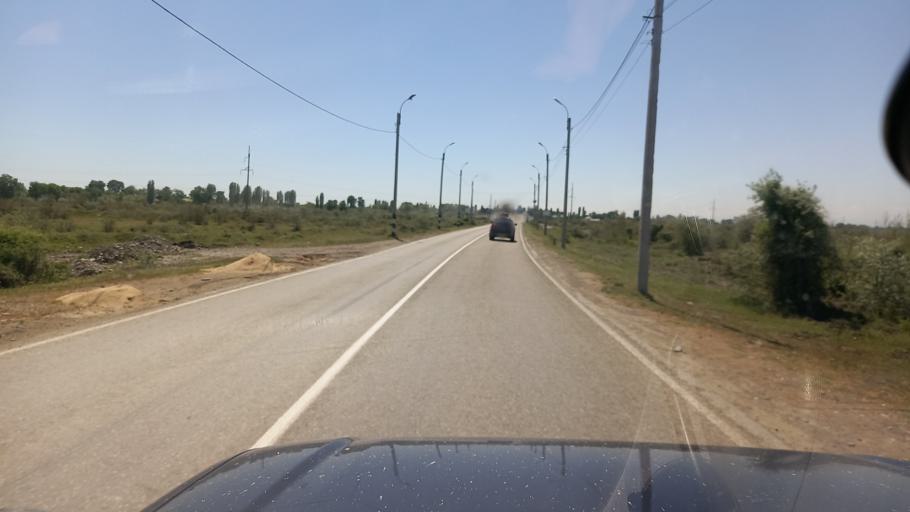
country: RU
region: Dagestan
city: Samur
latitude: 41.7353
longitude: 48.4519
